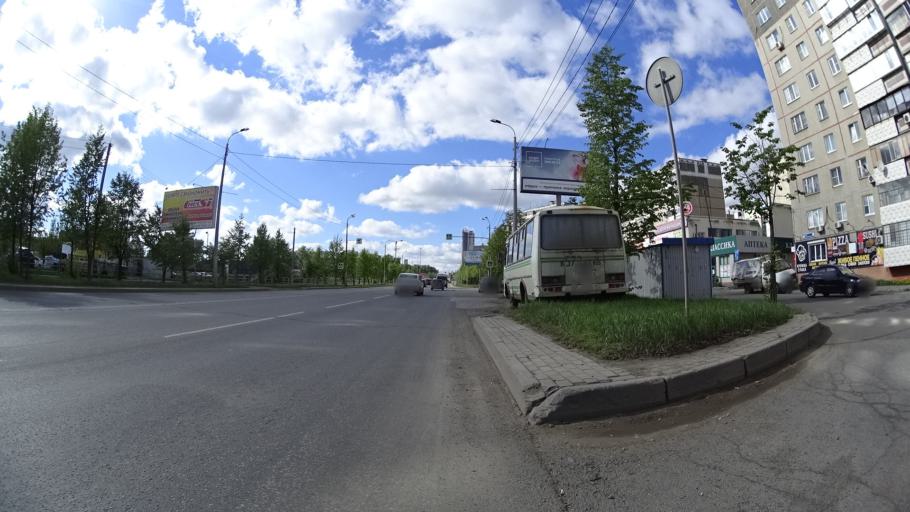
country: RU
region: Chelyabinsk
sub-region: Gorod Chelyabinsk
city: Chelyabinsk
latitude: 55.1722
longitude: 61.2935
